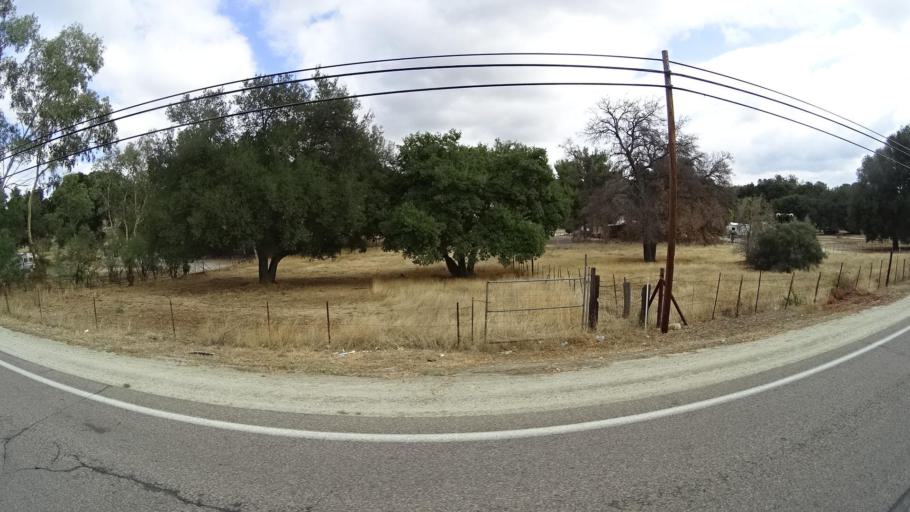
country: US
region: California
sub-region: San Diego County
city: Campo
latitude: 32.6520
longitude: -116.4875
